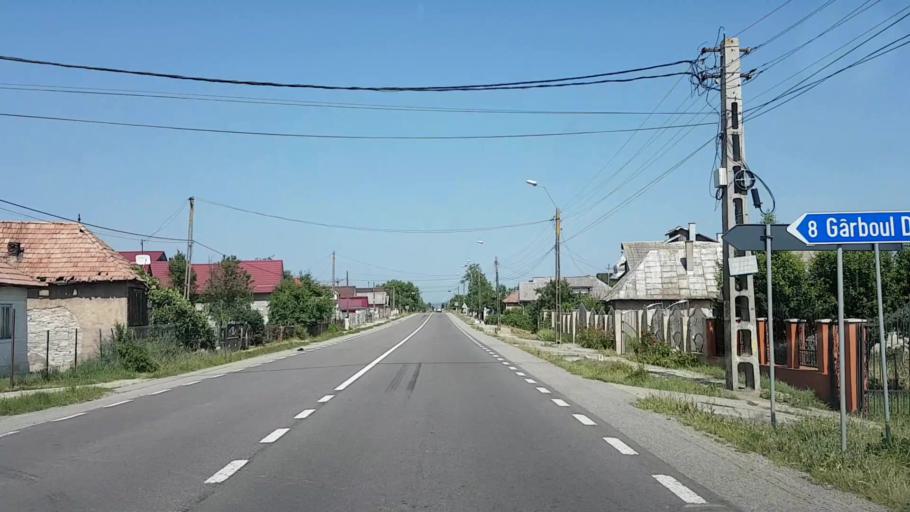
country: RO
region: Cluj
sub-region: Comuna Cusdrioara
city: Cusdrioara
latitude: 47.1758
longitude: 23.9409
